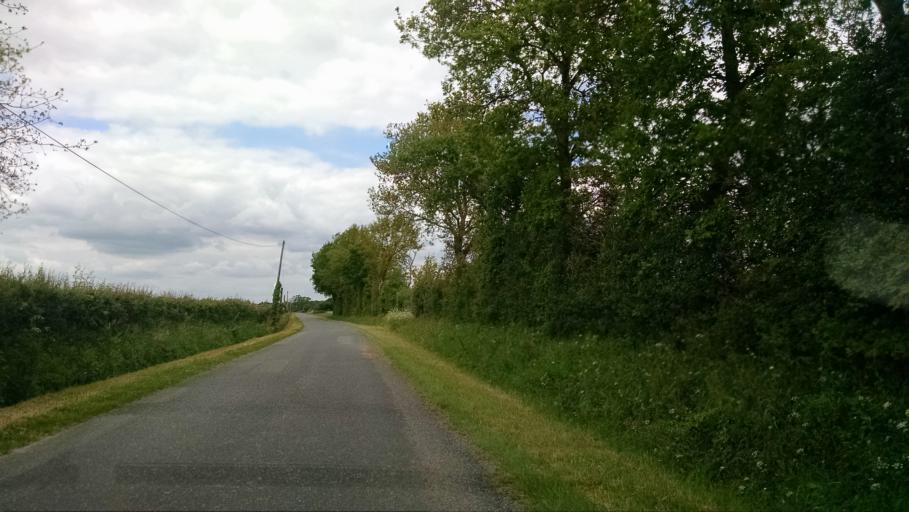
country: FR
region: Pays de la Loire
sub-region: Departement de la Loire-Atlantique
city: Remouille
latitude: 47.0192
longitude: -1.3805
